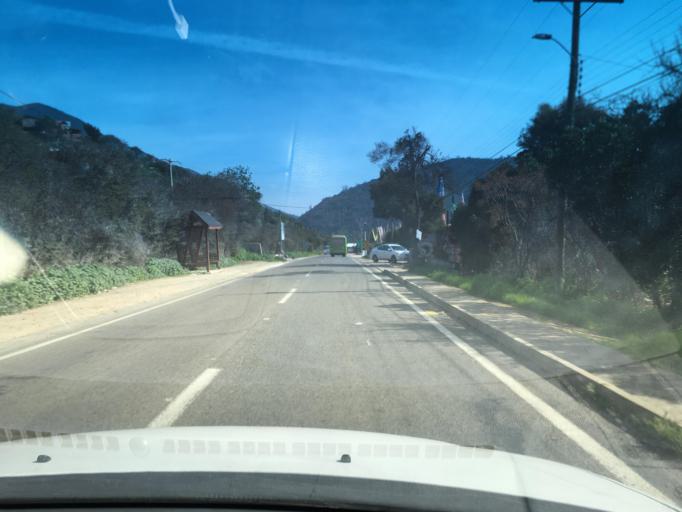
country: CL
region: Valparaiso
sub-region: Provincia de Marga Marga
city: Limache
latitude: -33.0517
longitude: -71.0988
